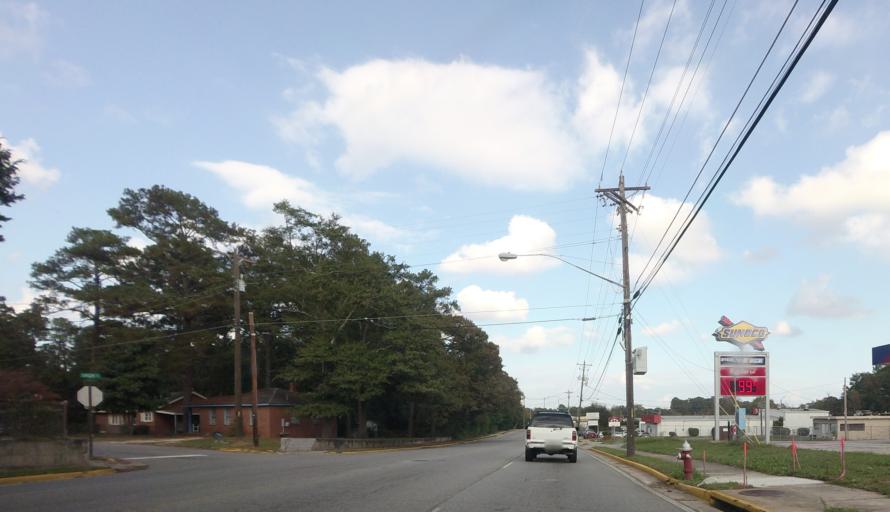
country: US
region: Georgia
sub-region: Houston County
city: Warner Robins
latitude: 32.6285
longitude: -83.6156
